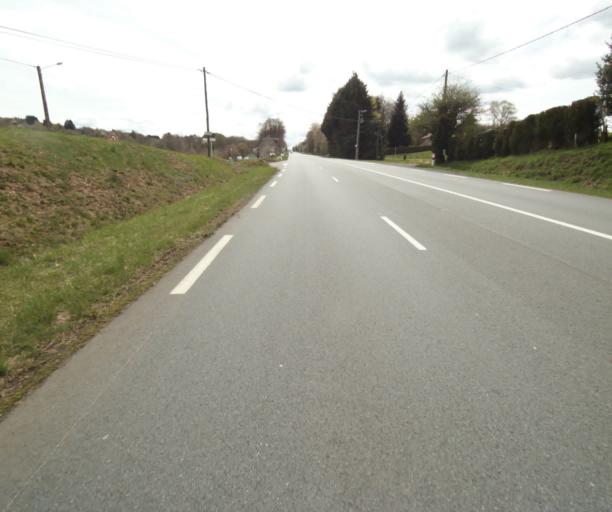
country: FR
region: Limousin
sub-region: Departement de la Correze
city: Sainte-Fortunade
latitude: 45.2062
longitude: 1.8272
